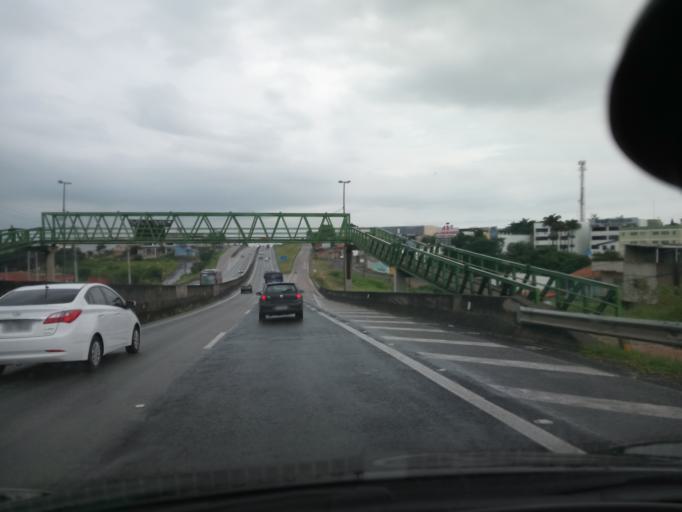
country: BR
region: Sao Paulo
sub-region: Campinas
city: Campinas
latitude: -22.9390
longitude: -47.0862
